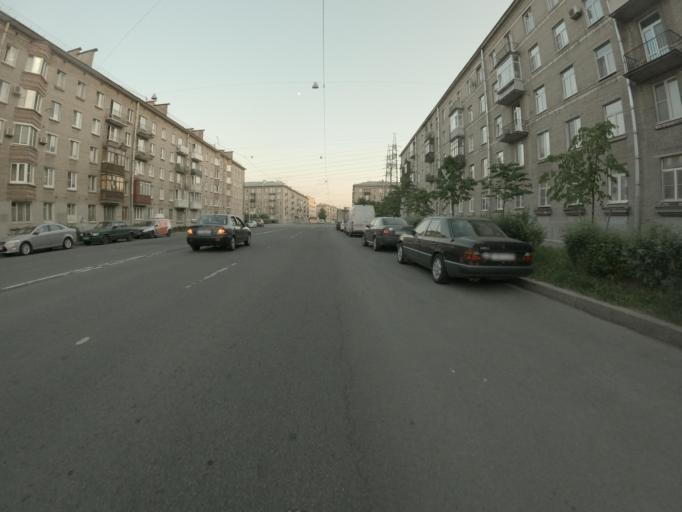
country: RU
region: St.-Petersburg
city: Avtovo
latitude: 59.8754
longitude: 30.2701
